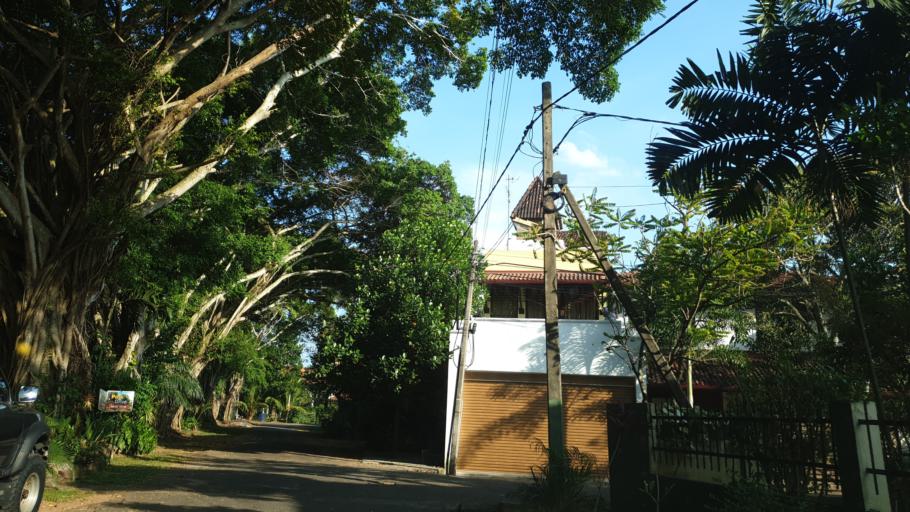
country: LK
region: Western
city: Galkissa
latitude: 6.8456
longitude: 79.8804
